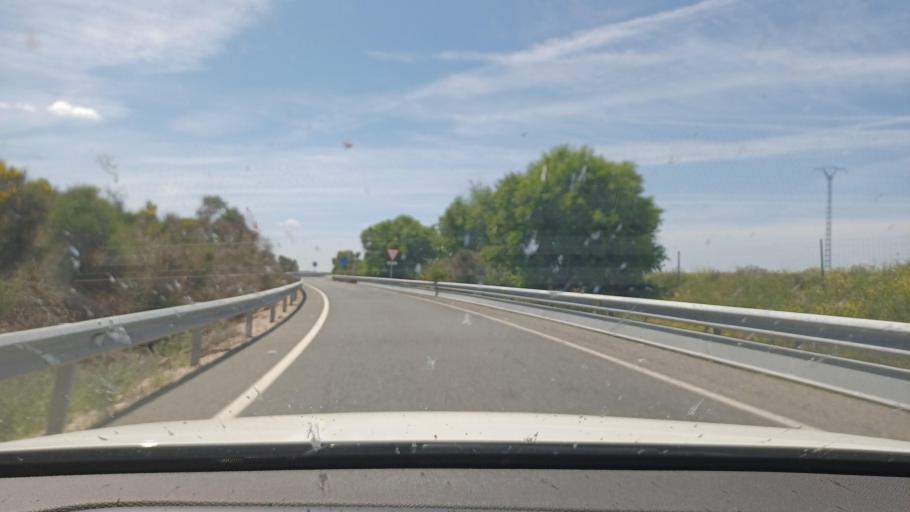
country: ES
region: Castille-La Mancha
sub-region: Provincia de Cuenca
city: Montalbo
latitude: 39.8882
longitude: -2.6839
